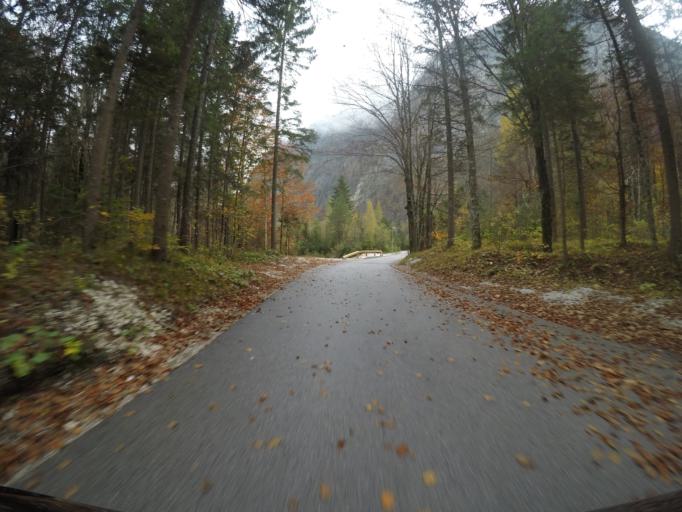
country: SI
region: Kranjska Gora
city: Mojstrana
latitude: 46.4305
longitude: 13.9453
